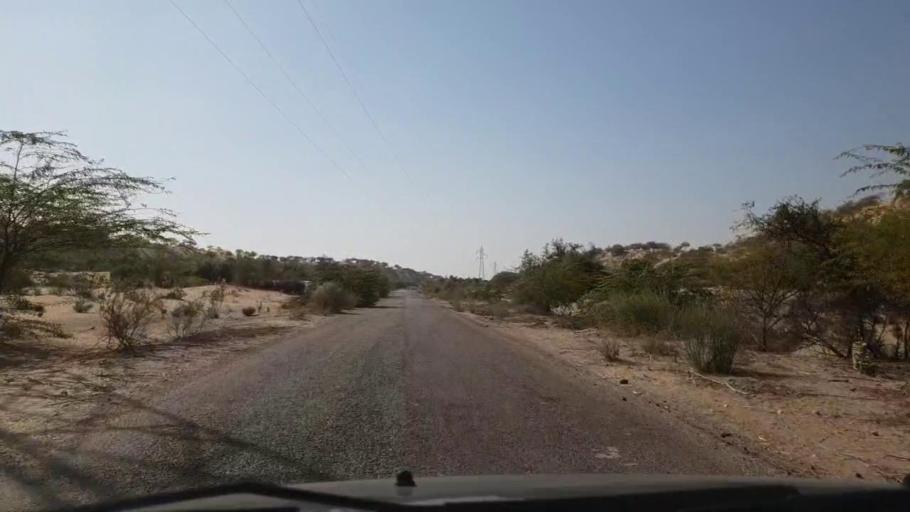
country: PK
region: Sindh
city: Diplo
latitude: 24.5791
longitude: 69.6981
